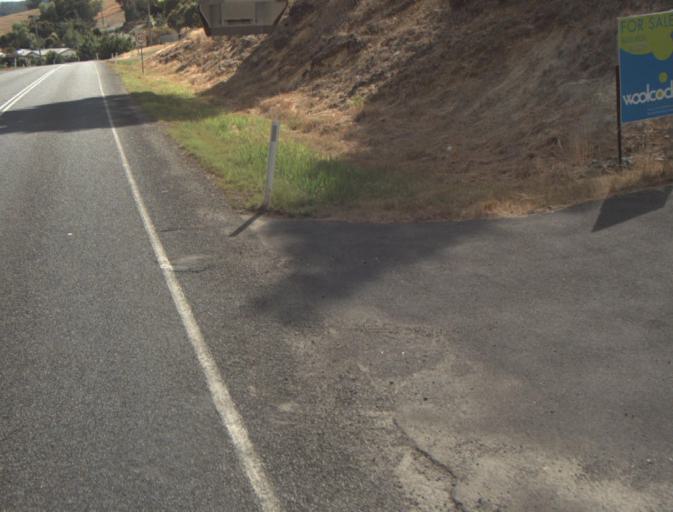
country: AU
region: Tasmania
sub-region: Launceston
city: Mayfield
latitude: -41.2642
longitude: 147.2163
